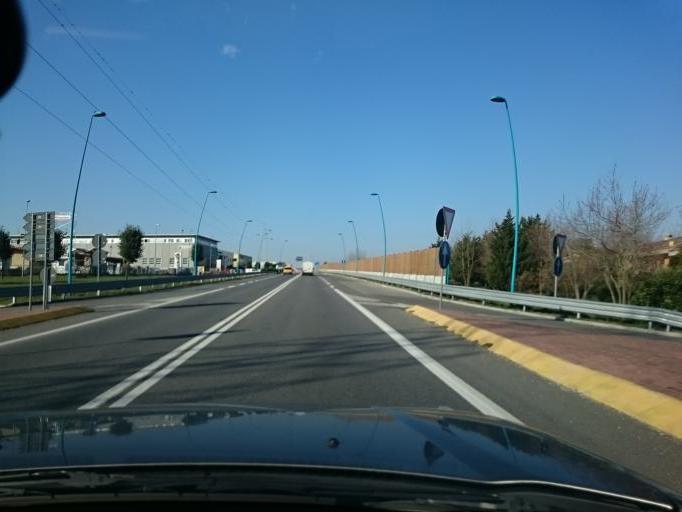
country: IT
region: Veneto
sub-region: Provincia di Verona
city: Peschiera del Garda
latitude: 45.4311
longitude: 10.6958
